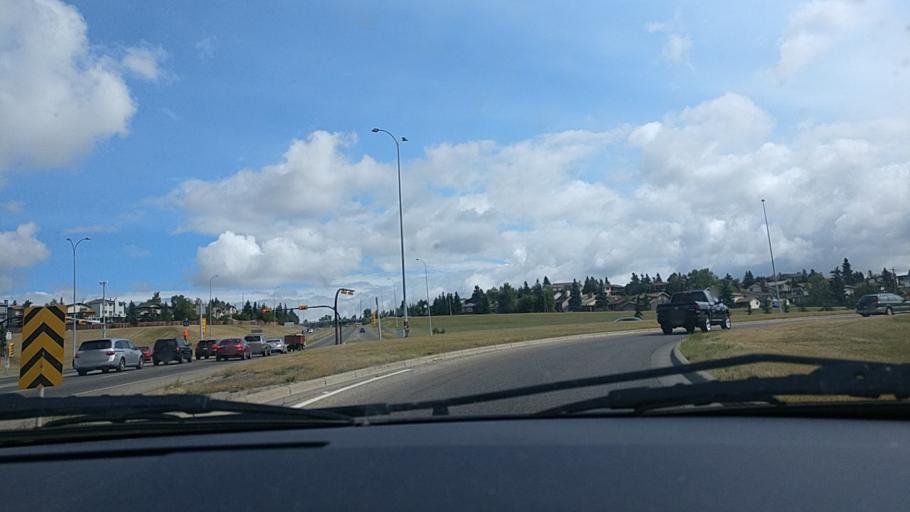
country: CA
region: Alberta
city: Calgary
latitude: 51.1200
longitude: -114.1671
